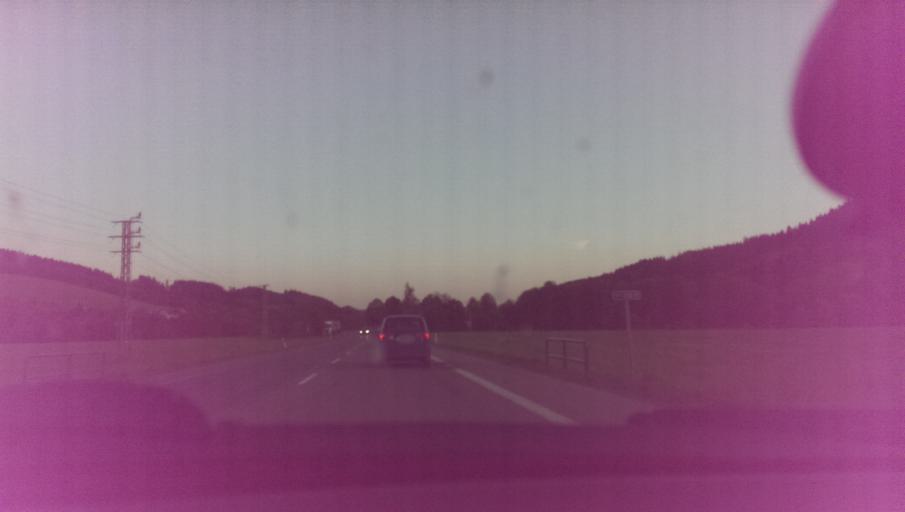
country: CZ
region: Zlin
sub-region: Okres Vsetin
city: Vsetin
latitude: 49.3144
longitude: 18.0048
